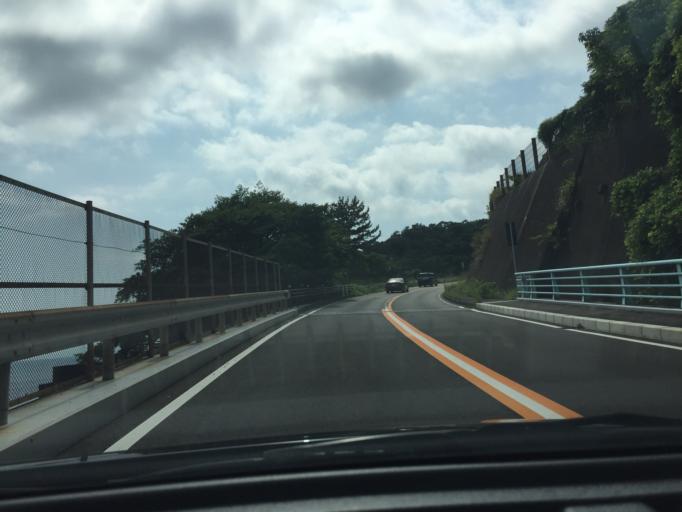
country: JP
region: Shizuoka
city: Ito
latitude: 34.9716
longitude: 139.1217
